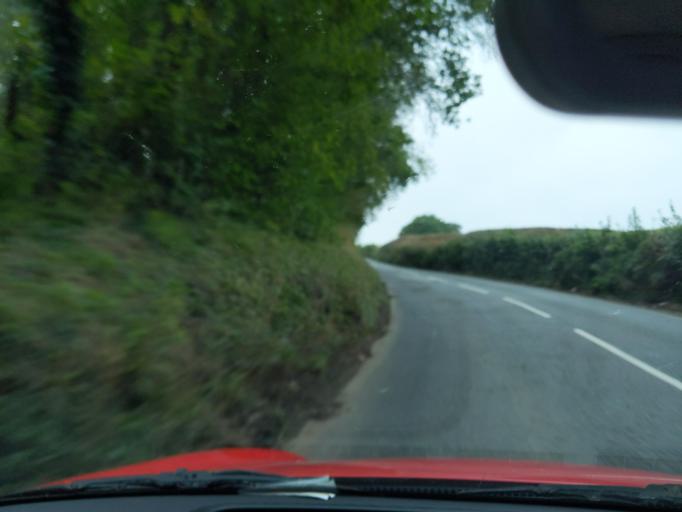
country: GB
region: England
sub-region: Devon
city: Okehampton
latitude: 50.8398
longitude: -4.0765
